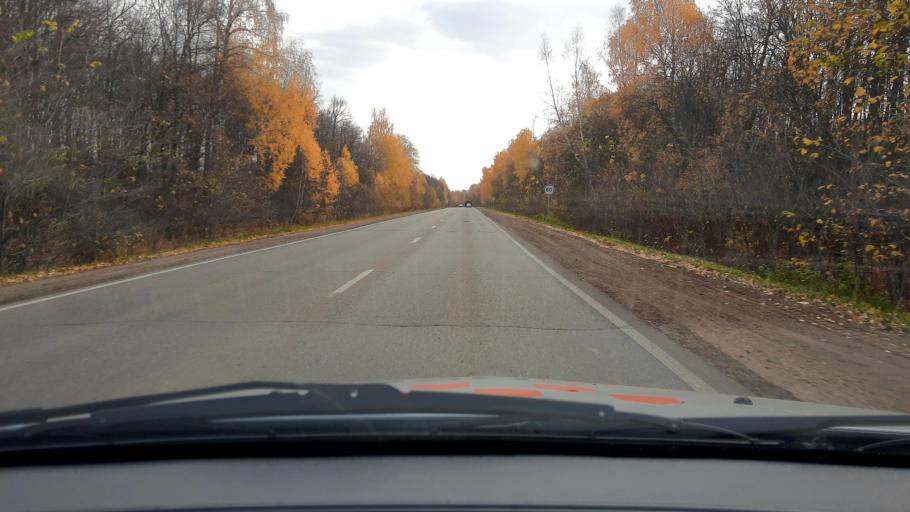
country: RU
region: Bashkortostan
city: Avdon
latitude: 54.8204
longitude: 55.7243
